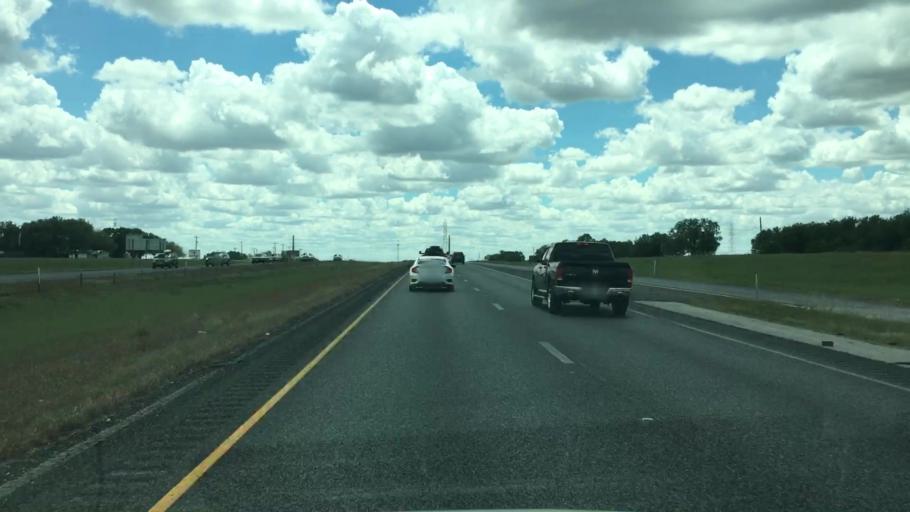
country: US
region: Texas
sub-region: Bexar County
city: Elmendorf
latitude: 29.2770
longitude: -98.3961
